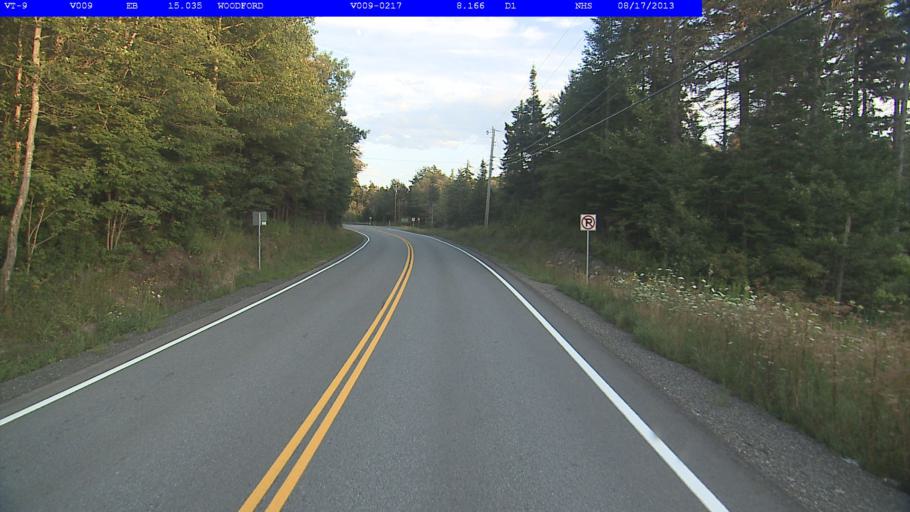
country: US
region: Vermont
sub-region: Bennington County
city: Bennington
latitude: 42.8932
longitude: -73.0364
